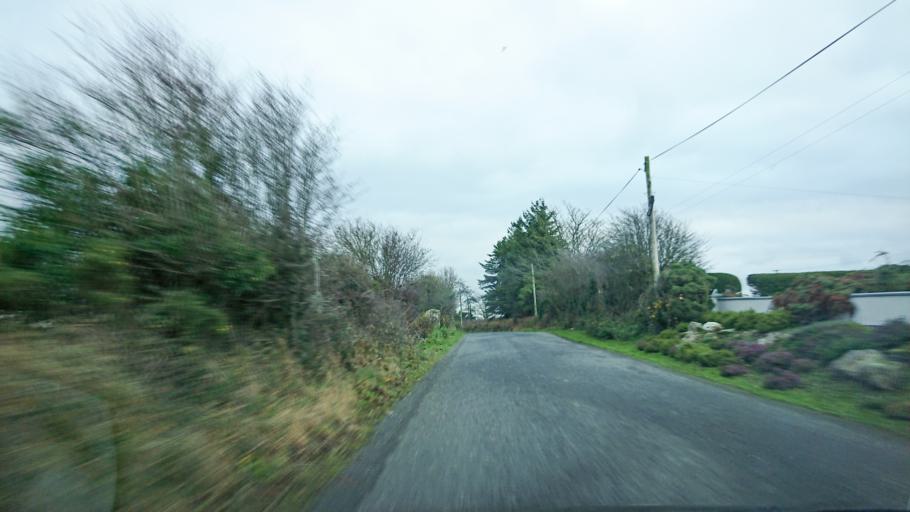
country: IE
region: Munster
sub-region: Waterford
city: Dunmore East
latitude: 52.2384
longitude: -6.9893
